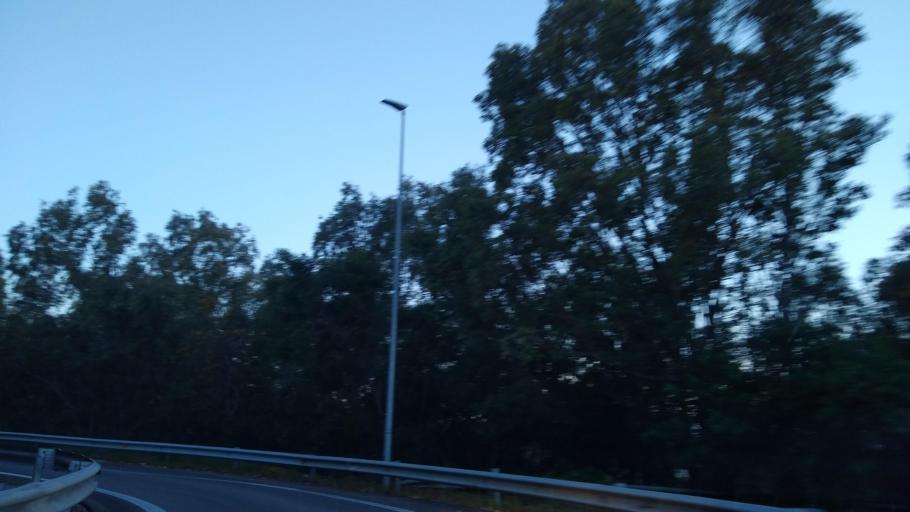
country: IT
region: Sicily
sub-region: Trapani
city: Alcamo
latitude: 38.0174
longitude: 12.9570
